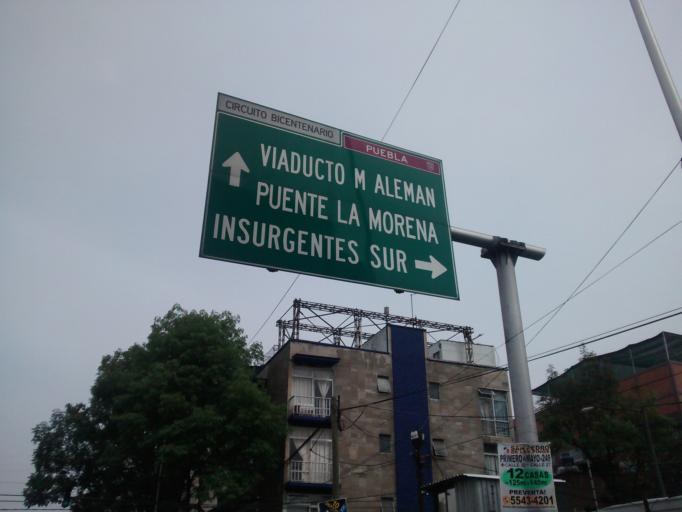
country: MX
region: Mexico City
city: Colonia del Valle
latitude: 19.3885
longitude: -99.1824
